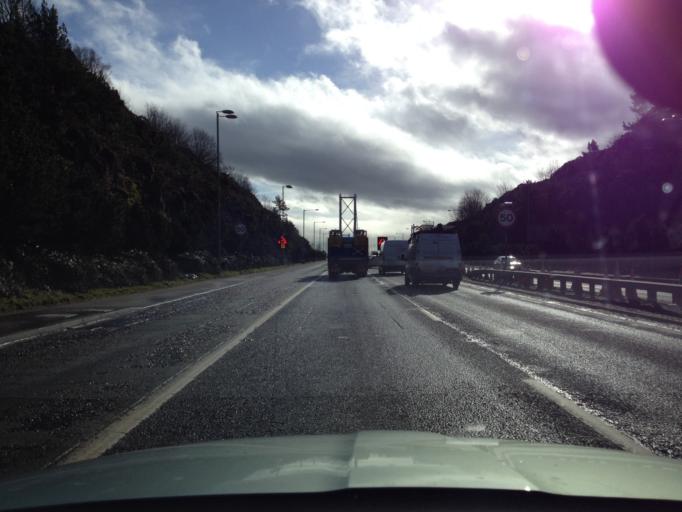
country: GB
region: Scotland
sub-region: Fife
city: North Queensferry
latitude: 56.0151
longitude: -3.4032
